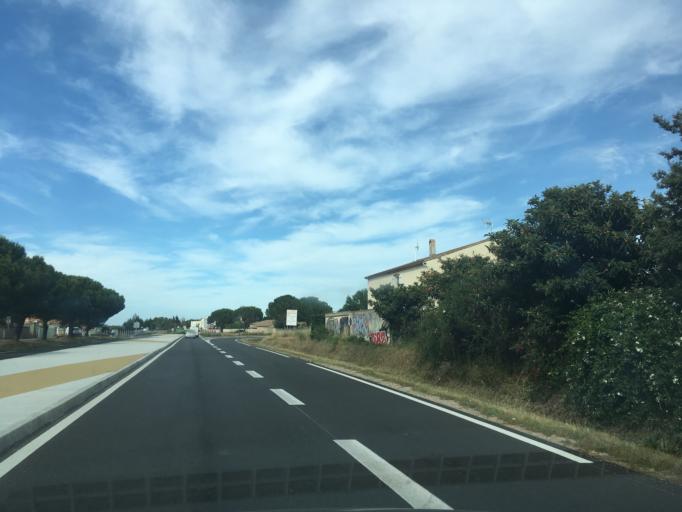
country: FR
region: Languedoc-Roussillon
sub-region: Departement du Gard
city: Garons
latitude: 43.7752
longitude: 4.4264
